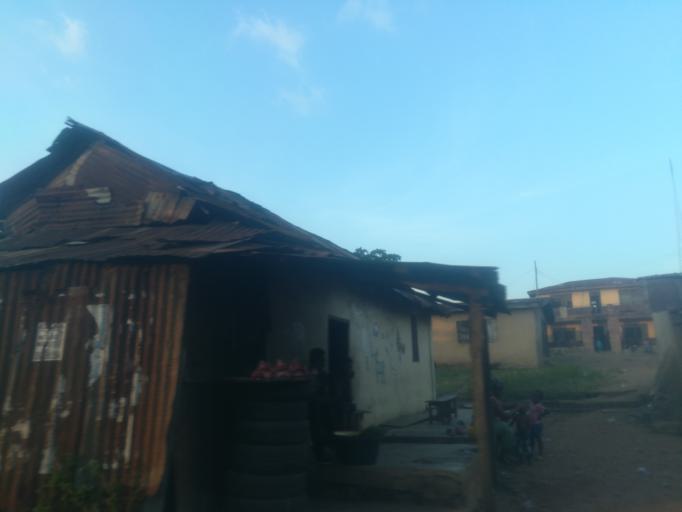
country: NG
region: Ogun
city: Abeokuta
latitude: 7.1495
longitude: 3.3320
